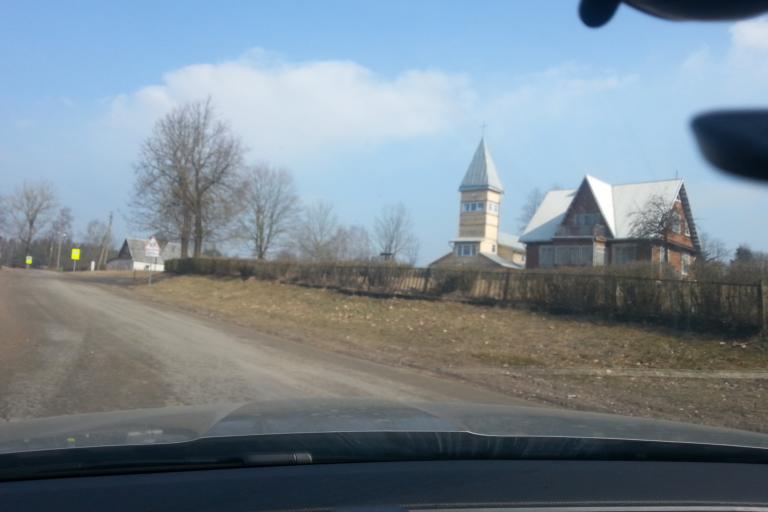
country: LT
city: Trakai
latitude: 54.5013
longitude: 24.9844
